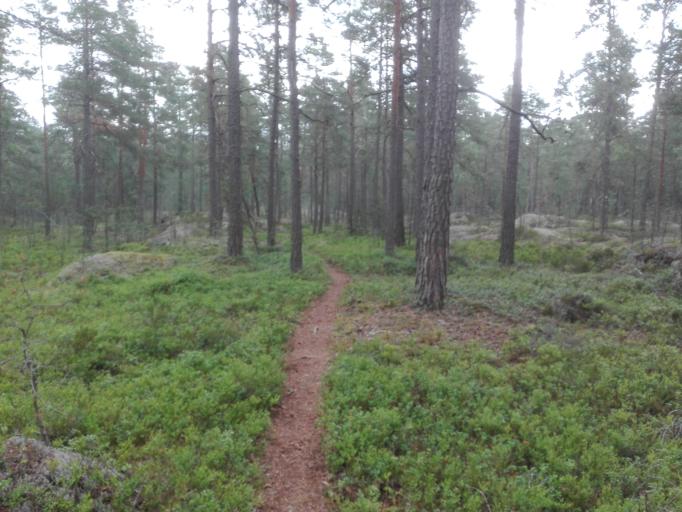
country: SE
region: Stockholm
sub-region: Nacka Kommun
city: Fisksatra
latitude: 59.2807
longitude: 18.2348
